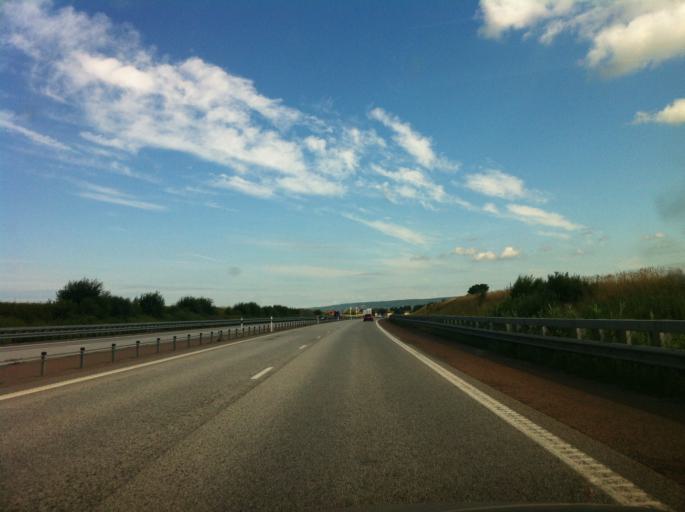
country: SE
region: Skane
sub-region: Angelholms Kommun
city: AEngelholm
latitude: 56.2607
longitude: 12.8957
